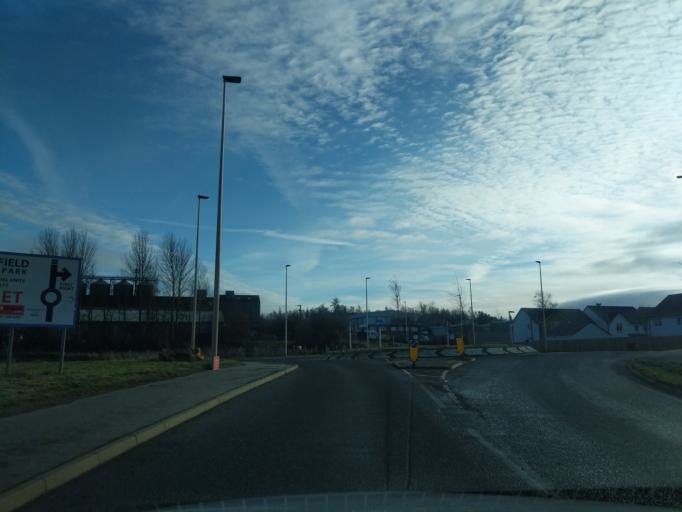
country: GB
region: Scotland
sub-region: Midlothian
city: Loanhead
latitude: 55.8859
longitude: -3.1506
